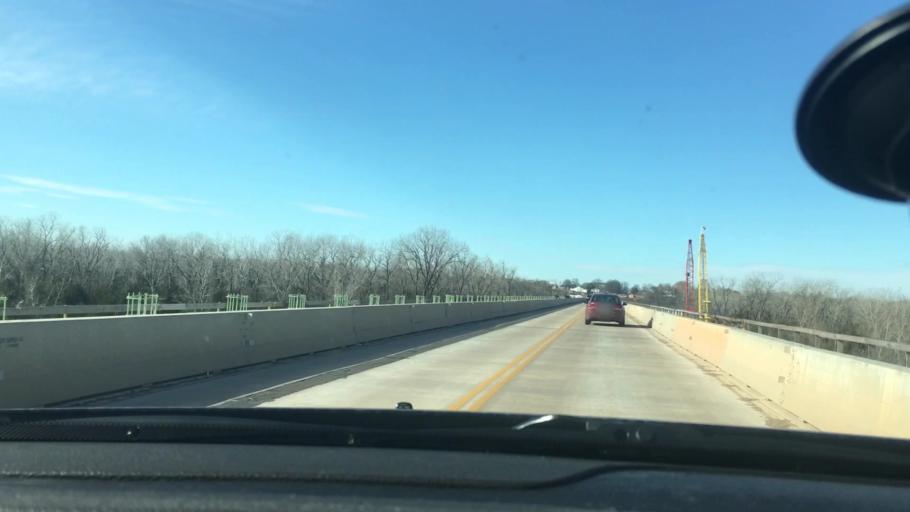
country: US
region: Oklahoma
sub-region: Cleveland County
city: Lexington
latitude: 35.0146
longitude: -97.3472
